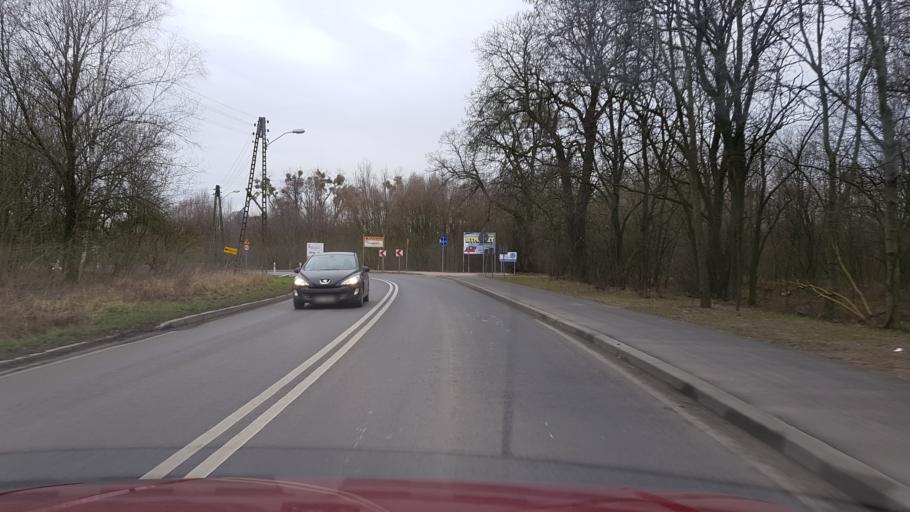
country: PL
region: West Pomeranian Voivodeship
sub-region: Powiat policki
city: Police
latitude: 53.5895
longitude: 14.5468
